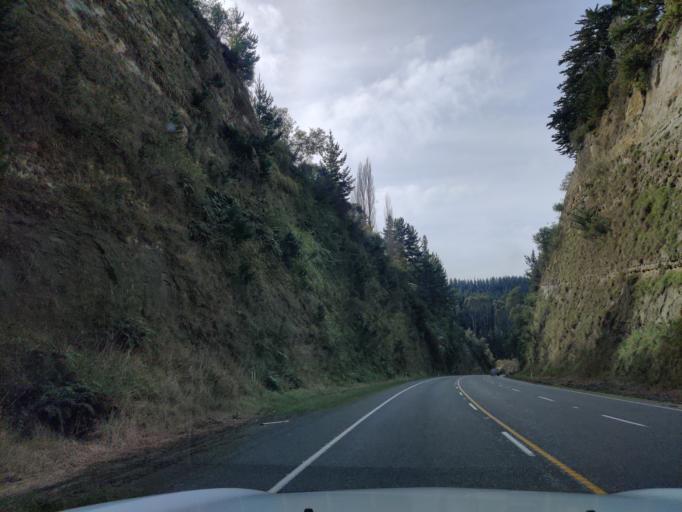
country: NZ
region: Manawatu-Wanganui
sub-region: Ruapehu District
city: Waiouru
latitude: -39.7590
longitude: 175.8077
